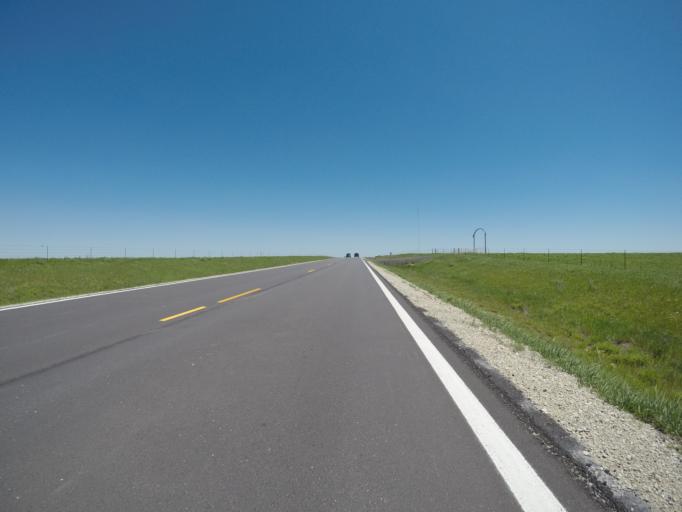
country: US
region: Kansas
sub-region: Chase County
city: Cottonwood Falls
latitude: 38.5041
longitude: -96.5512
